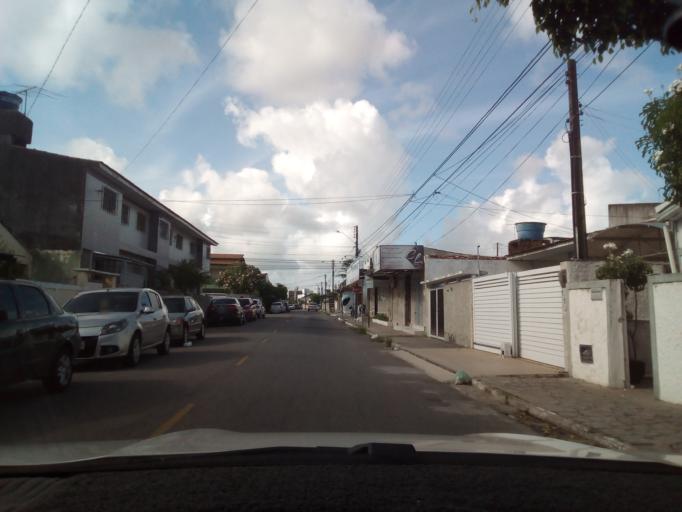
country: BR
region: Paraiba
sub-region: Joao Pessoa
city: Joao Pessoa
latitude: -7.1346
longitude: -34.8756
